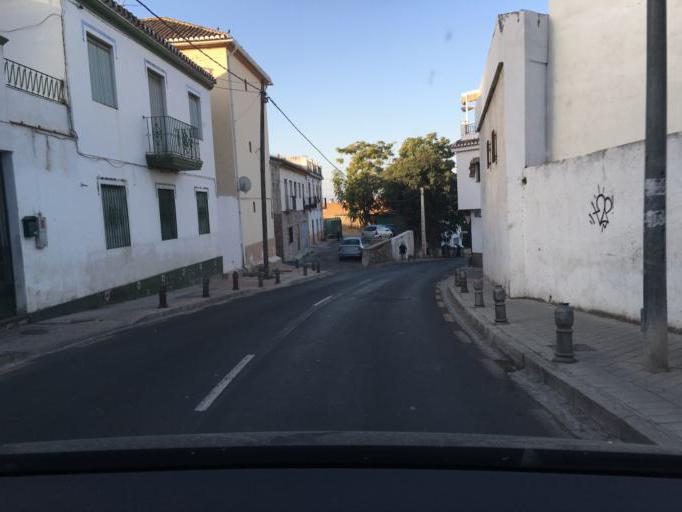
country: ES
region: Andalusia
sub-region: Provincia de Granada
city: Granada
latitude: 37.1880
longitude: -3.5904
